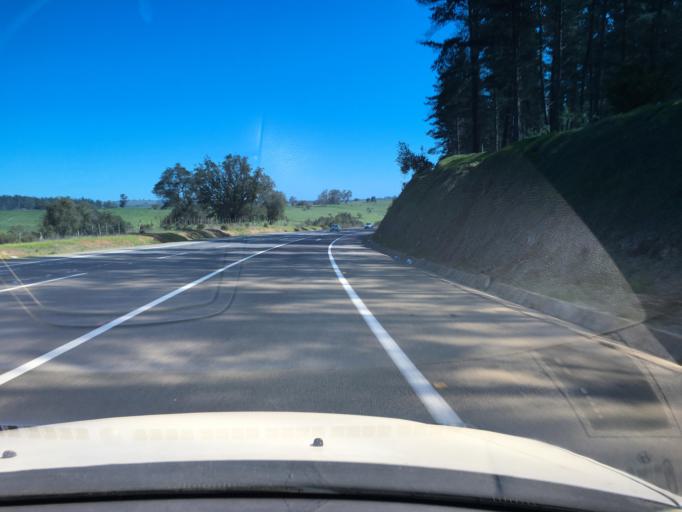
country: CL
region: Valparaiso
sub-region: San Antonio Province
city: El Tabo
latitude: -33.4095
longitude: -71.5129
